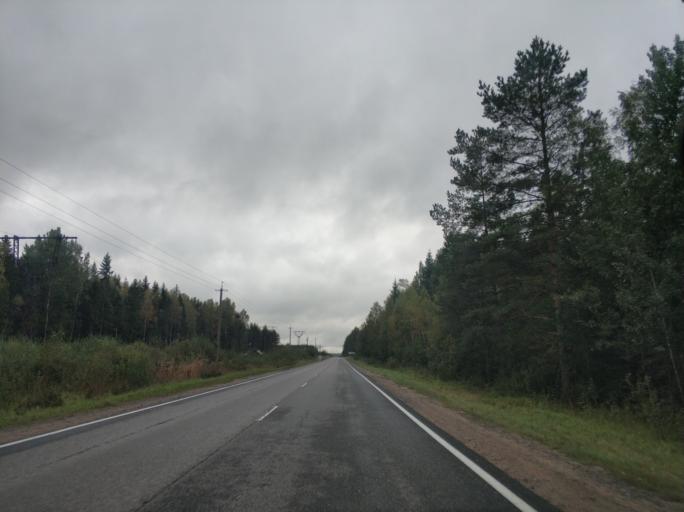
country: RU
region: Leningrad
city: Borisova Griva
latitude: 60.1018
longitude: 30.9564
